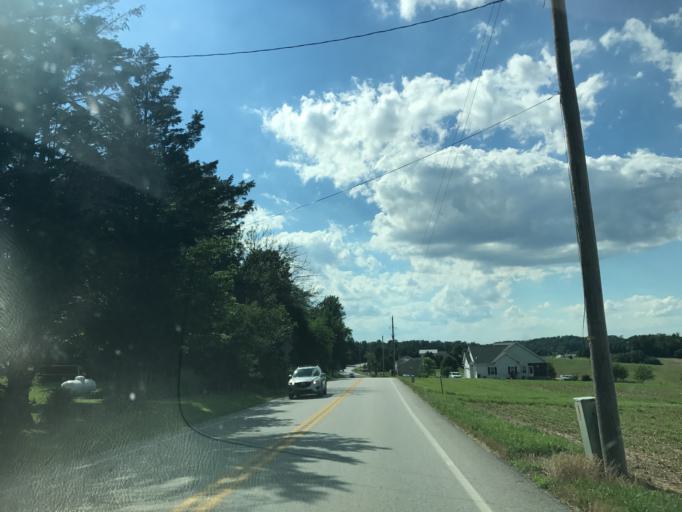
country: US
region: Pennsylvania
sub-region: York County
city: New Freedom
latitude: 39.7296
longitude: -76.7686
